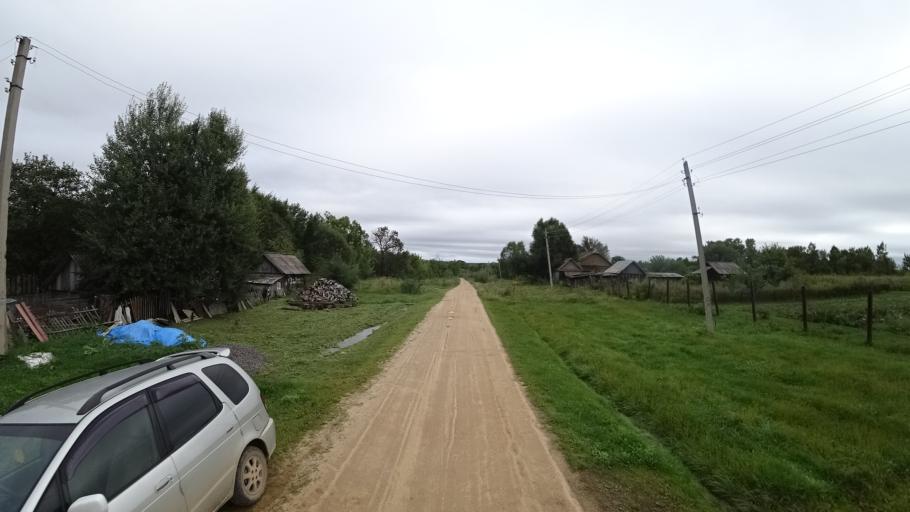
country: RU
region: Primorskiy
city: Rettikhovka
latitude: 44.1394
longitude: 132.6372
